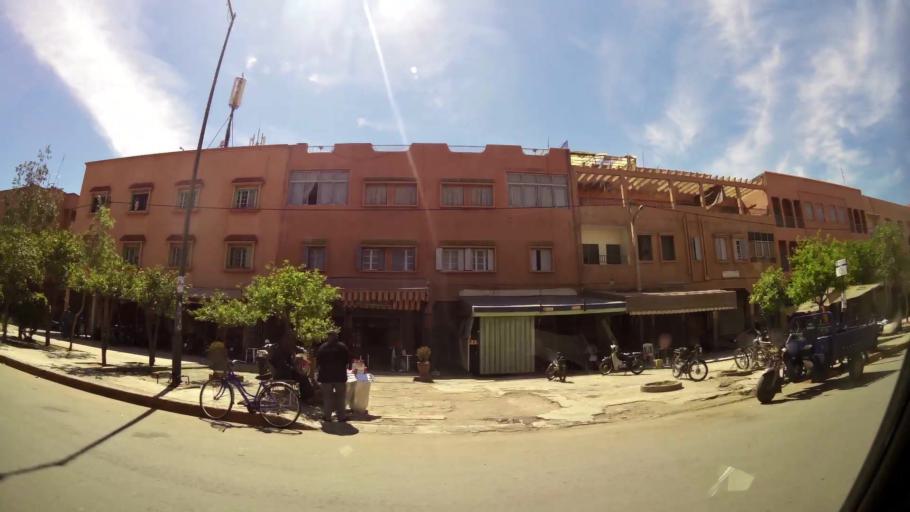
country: MA
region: Marrakech-Tensift-Al Haouz
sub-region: Marrakech
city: Marrakesh
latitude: 31.6068
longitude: -7.9702
